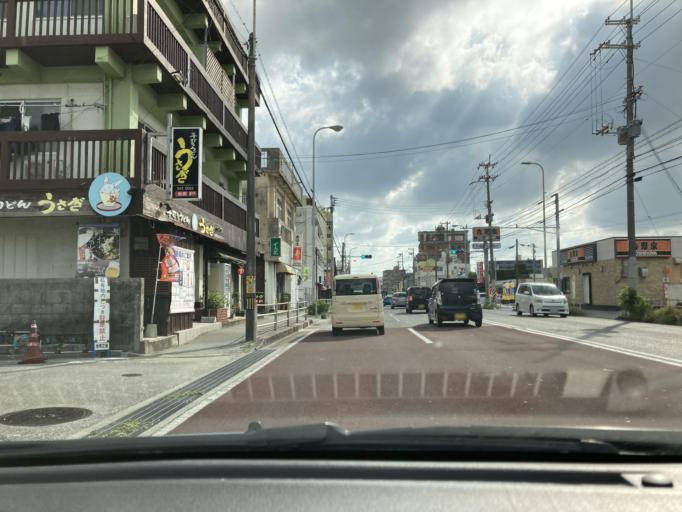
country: JP
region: Okinawa
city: Ginowan
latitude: 26.2095
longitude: 127.7586
